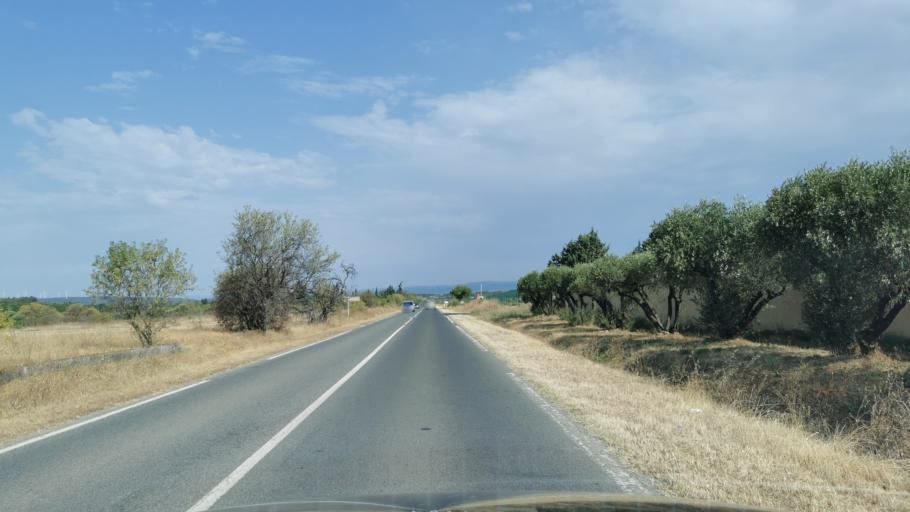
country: FR
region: Languedoc-Roussillon
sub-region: Departement de l'Aude
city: Ginestas
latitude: 43.2763
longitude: 2.8852
